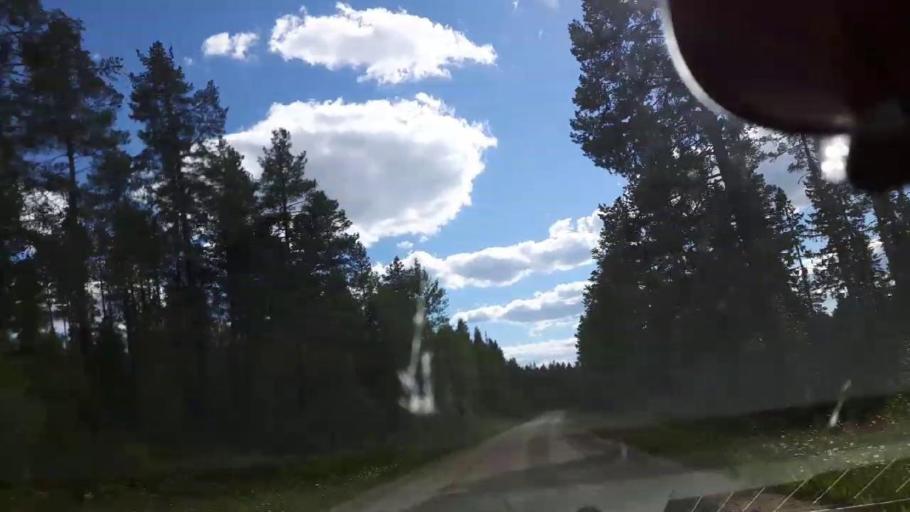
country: SE
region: Vaesternorrland
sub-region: Ange Kommun
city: Ange
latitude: 62.7309
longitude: 15.6452
